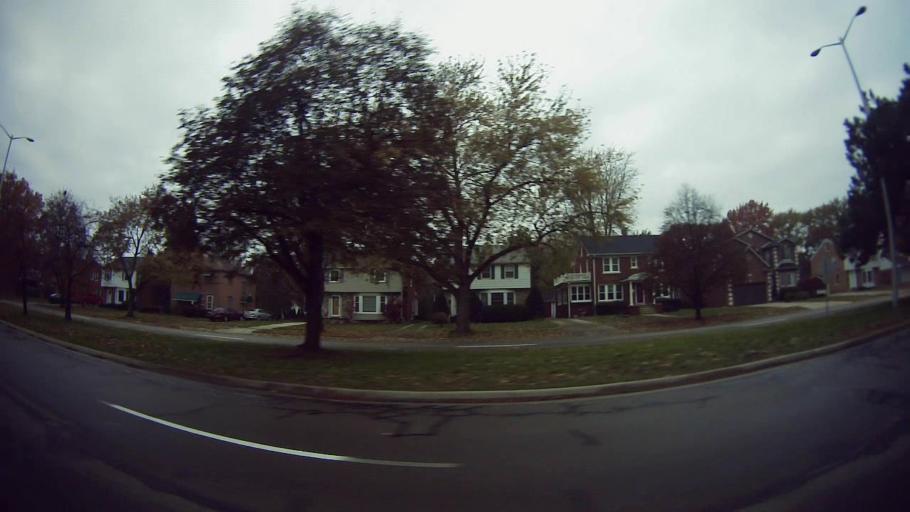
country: US
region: Michigan
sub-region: Wayne County
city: Dearborn Heights
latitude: 42.3157
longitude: -83.2545
